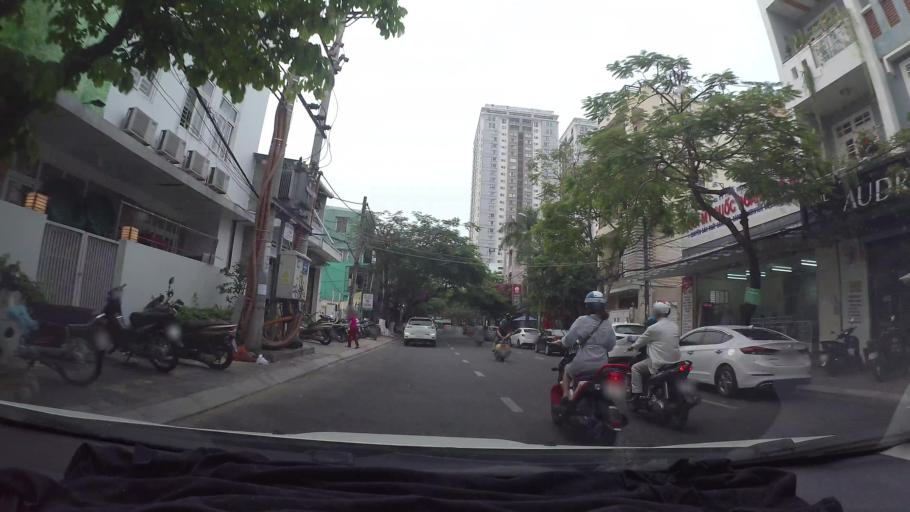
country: VN
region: Da Nang
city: Da Nang
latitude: 16.0788
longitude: 108.2201
